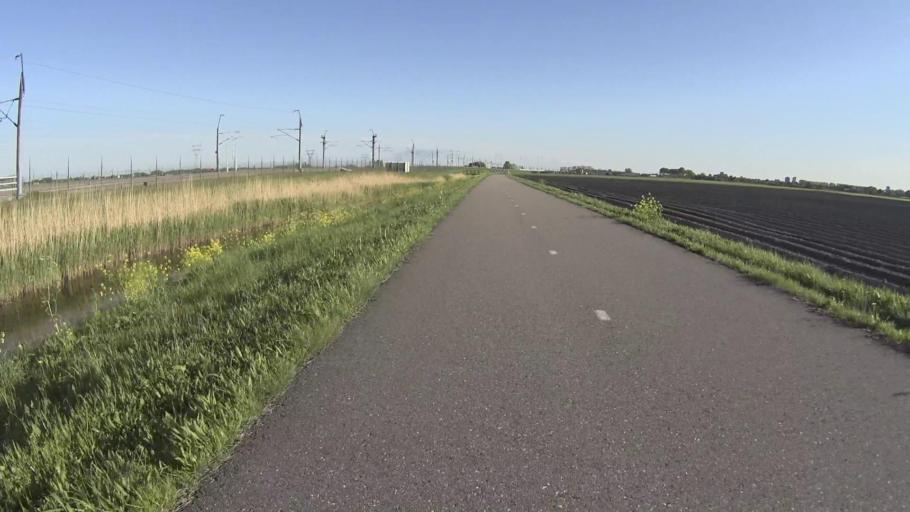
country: NL
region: South Holland
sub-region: Gemeente Rijnwoude
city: Benthuizen
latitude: 52.0893
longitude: 4.5647
